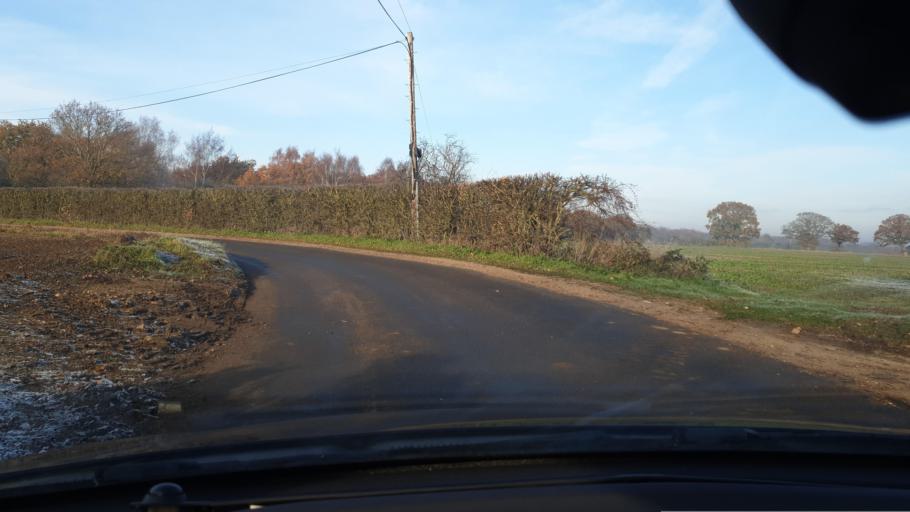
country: GB
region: England
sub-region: Essex
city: Mistley
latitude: 51.9771
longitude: 1.1175
